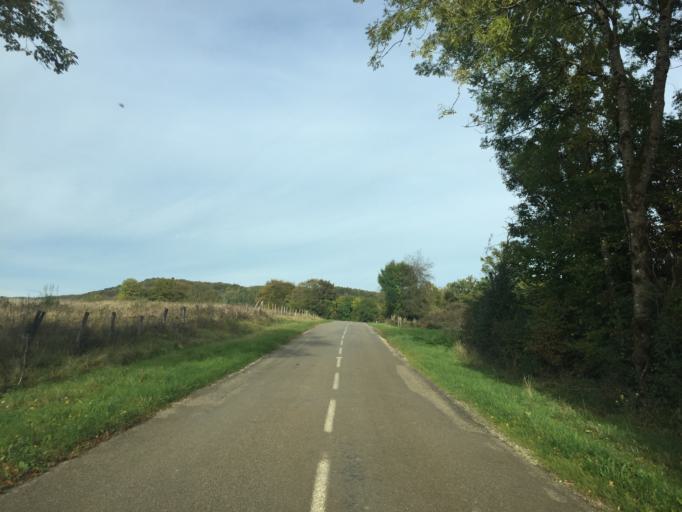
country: FR
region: Bourgogne
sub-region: Departement de Saone-et-Loire
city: Cuiseaux
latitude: 46.4945
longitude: 5.4988
